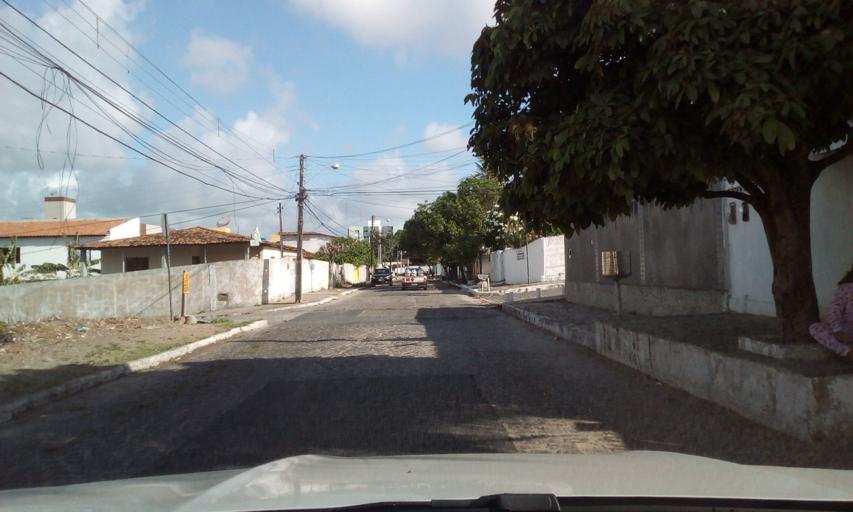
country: BR
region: Paraiba
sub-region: Joao Pessoa
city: Joao Pessoa
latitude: -7.1552
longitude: -34.8429
